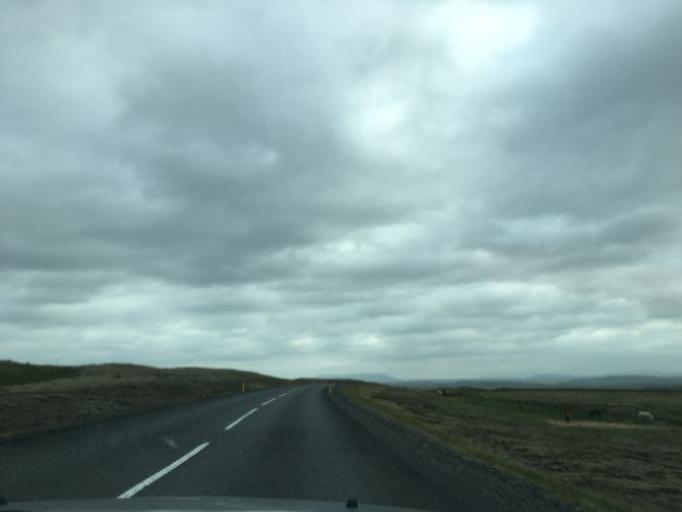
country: IS
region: South
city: Vestmannaeyjar
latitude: 64.2431
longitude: -20.2153
